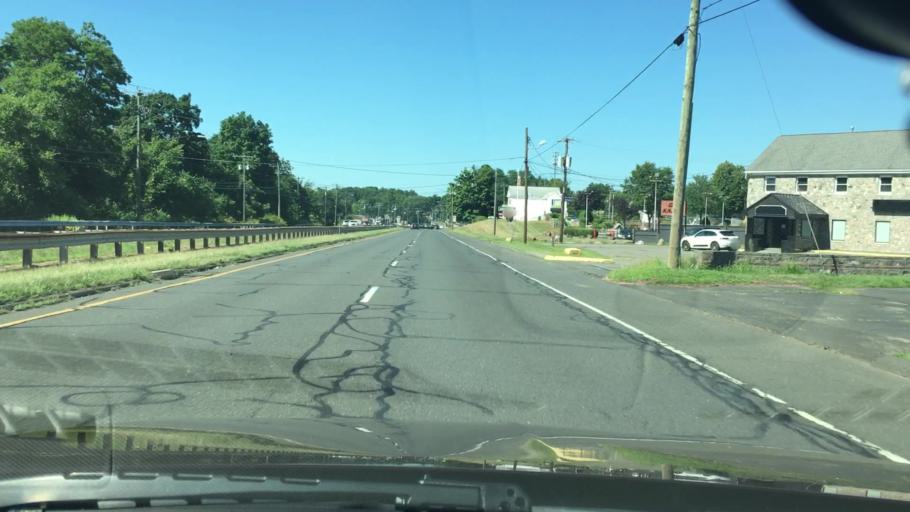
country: US
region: Connecticut
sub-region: Hartford County
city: Kensington
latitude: 41.6090
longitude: -72.7559
